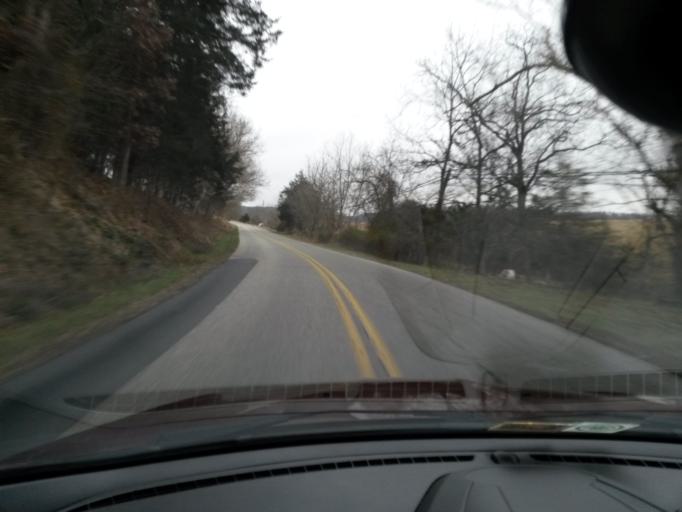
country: US
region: Virginia
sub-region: Rockbridge County
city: East Lexington
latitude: 37.8966
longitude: -79.3460
